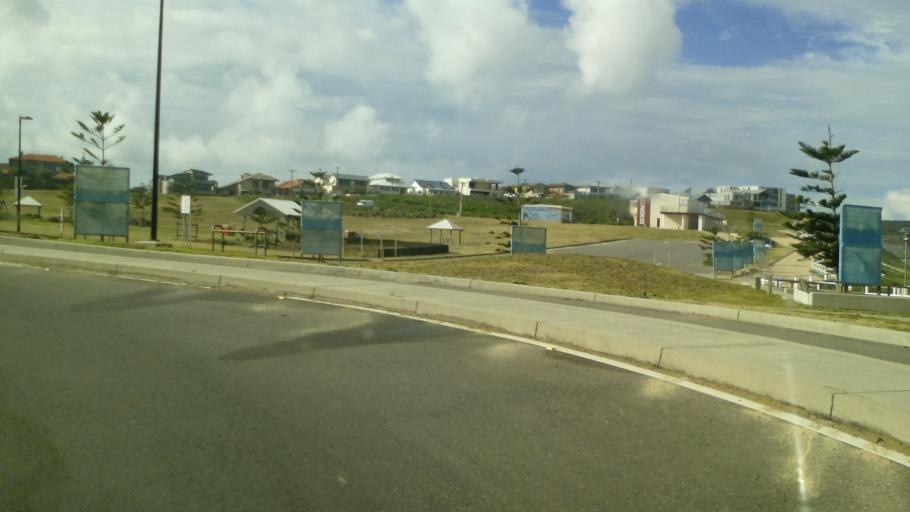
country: AU
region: New South Wales
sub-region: Newcastle
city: The Junction
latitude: -32.9467
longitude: 151.7588
